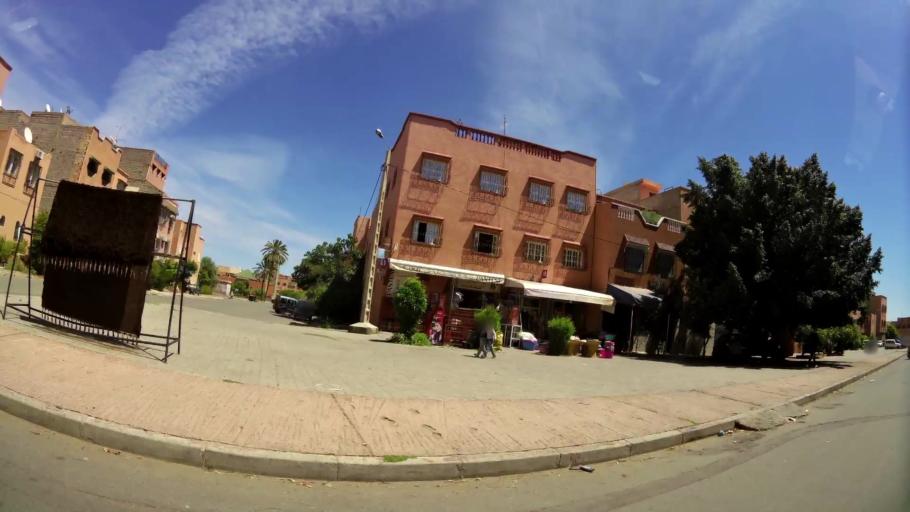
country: MA
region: Marrakech-Tensift-Al Haouz
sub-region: Marrakech
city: Marrakesh
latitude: 31.6396
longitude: -8.0543
